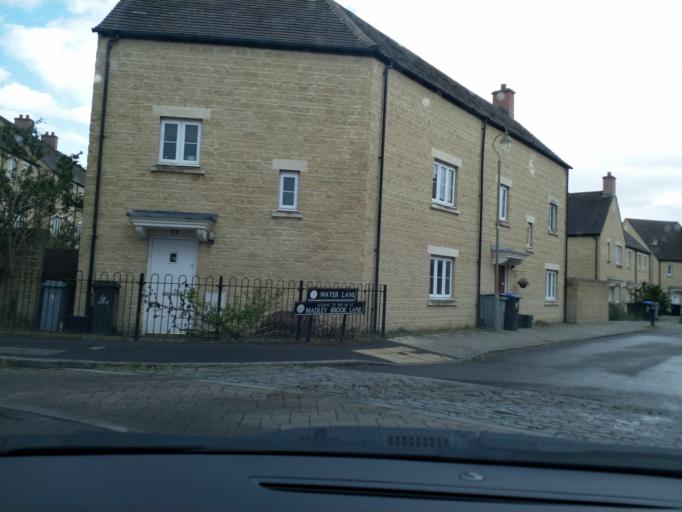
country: GB
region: England
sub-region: Oxfordshire
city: Witney
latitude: 51.7931
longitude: -1.4645
